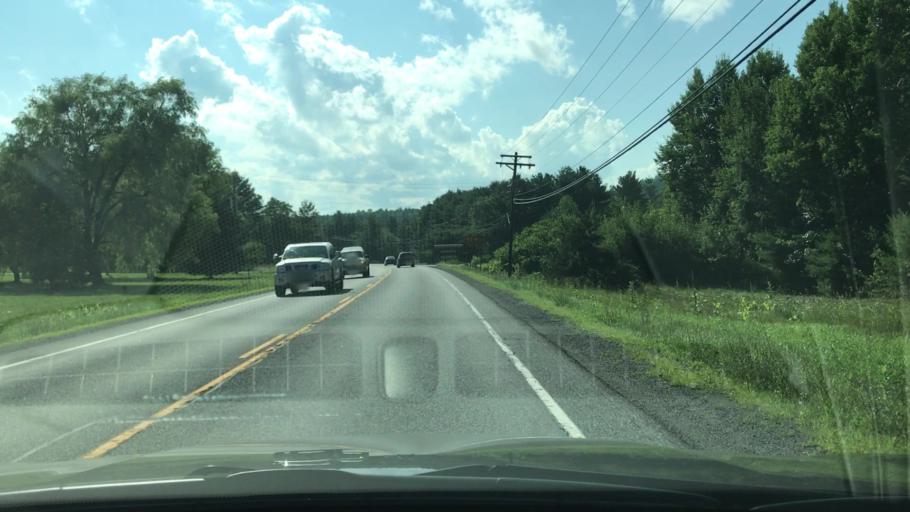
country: US
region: New York
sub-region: Warren County
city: Queensbury
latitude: 43.4042
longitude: -73.5942
